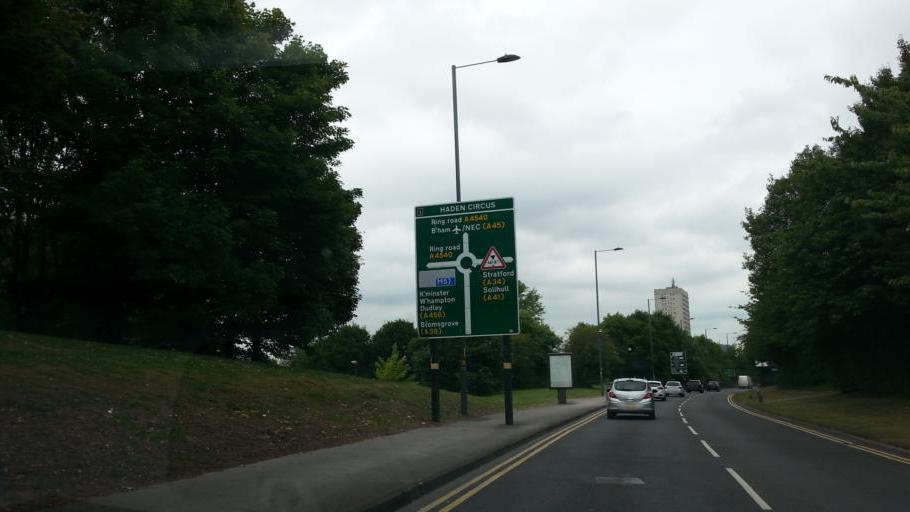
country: GB
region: England
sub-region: City and Borough of Birmingham
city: Birmingham
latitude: 52.4603
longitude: -1.8869
